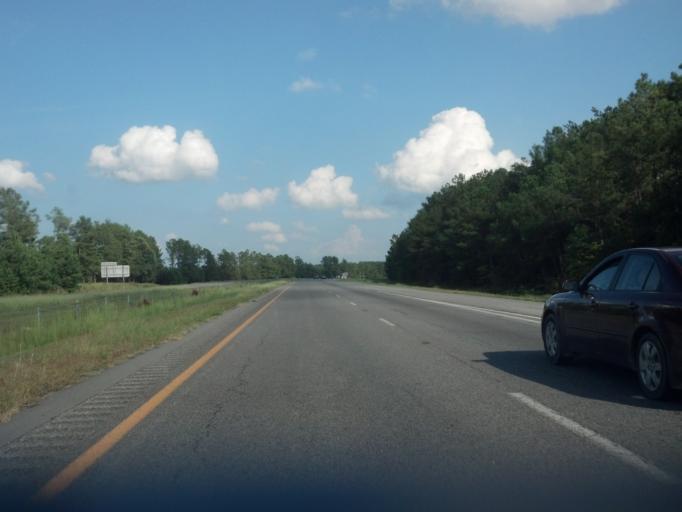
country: US
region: North Carolina
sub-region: Nash County
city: Rocky Mount
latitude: 35.9247
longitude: -77.6704
